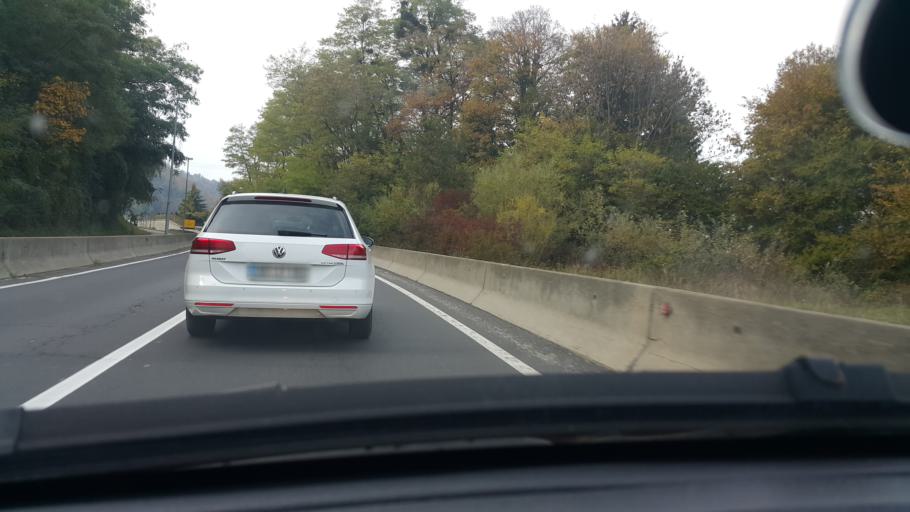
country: SI
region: Maribor
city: Kamnica
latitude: 46.5704
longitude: 15.6176
